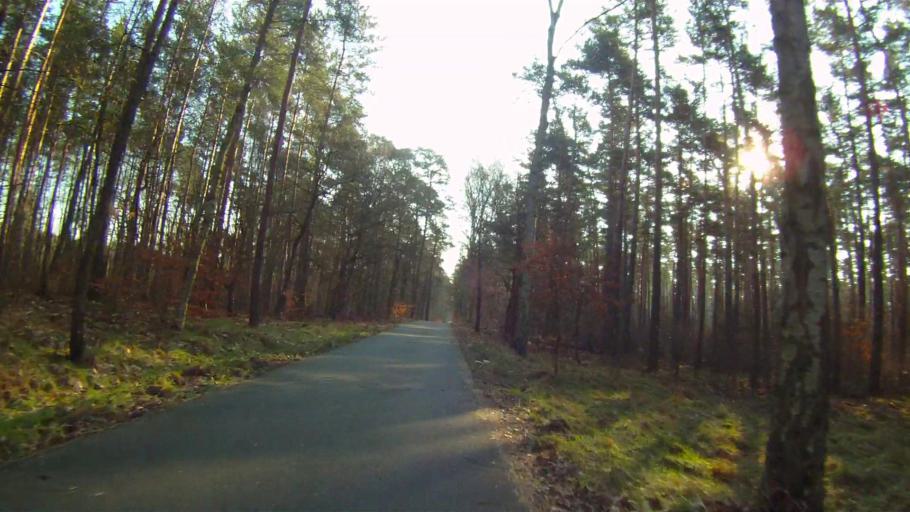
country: DE
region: Berlin
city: Rahnsdorf
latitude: 52.4202
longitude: 13.7089
